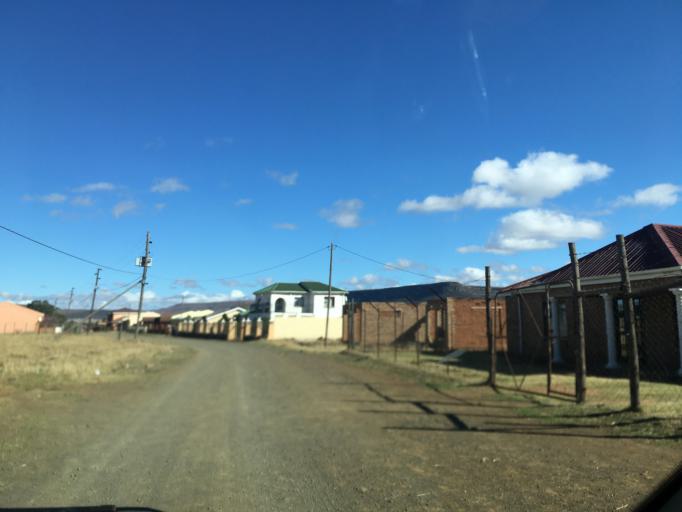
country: ZA
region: Eastern Cape
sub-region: Chris Hani District Municipality
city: Cala
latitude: -31.5348
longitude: 27.6943
